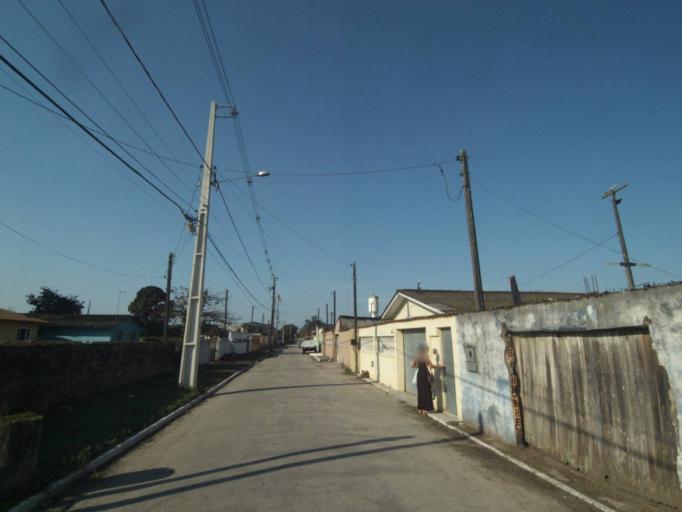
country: BR
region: Parana
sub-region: Paranagua
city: Paranagua
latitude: -25.5488
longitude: -48.5506
